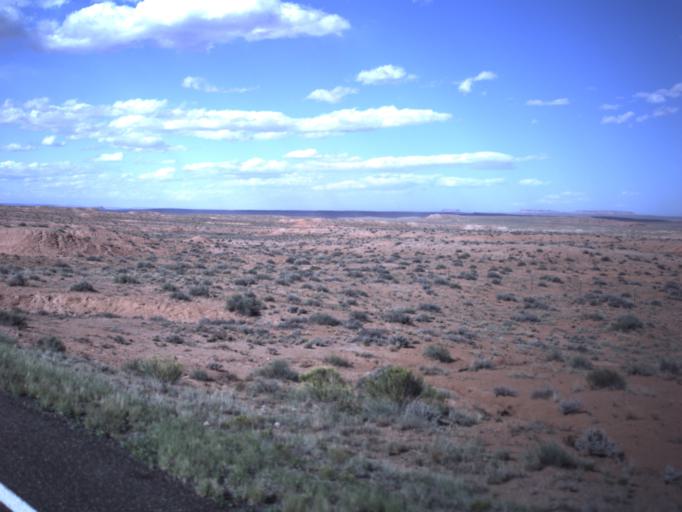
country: US
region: Utah
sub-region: Emery County
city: Ferron
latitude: 38.2994
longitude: -110.6685
